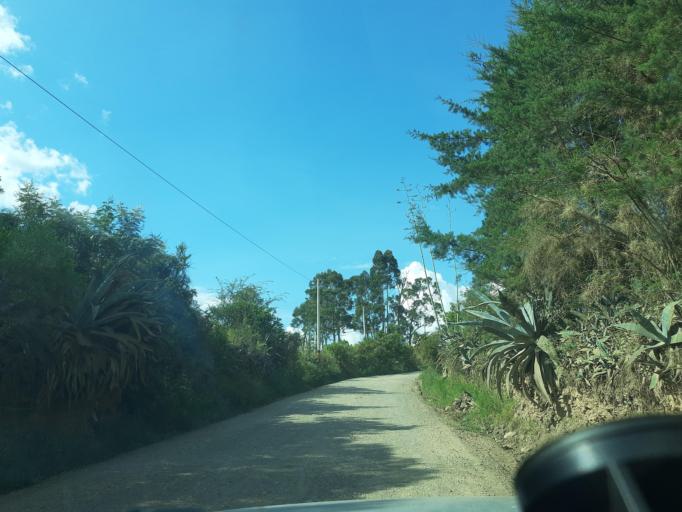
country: CO
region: Boyaca
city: Villa de Leiva
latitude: 5.6557
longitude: -73.5375
